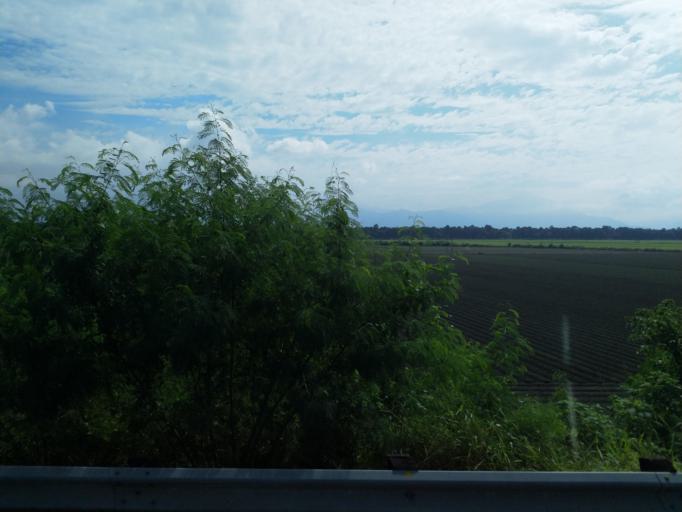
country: TW
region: Taiwan
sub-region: Pingtung
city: Pingtung
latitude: 22.8403
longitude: 120.4958
